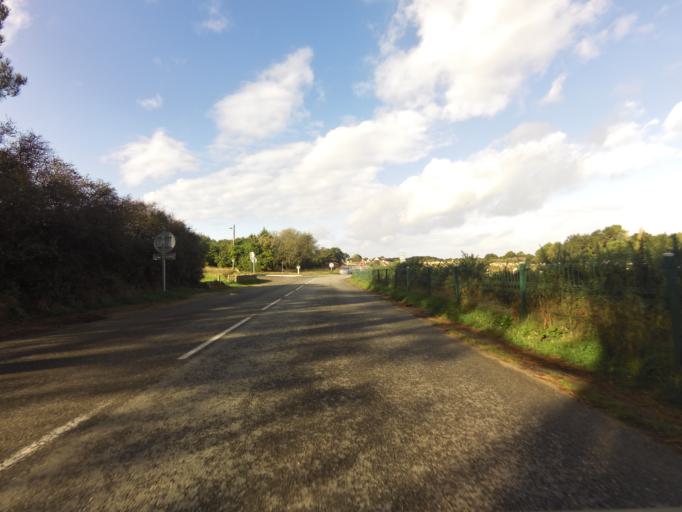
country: FR
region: Brittany
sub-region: Departement du Morbihan
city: Carnac
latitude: 47.5929
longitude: -3.0797
